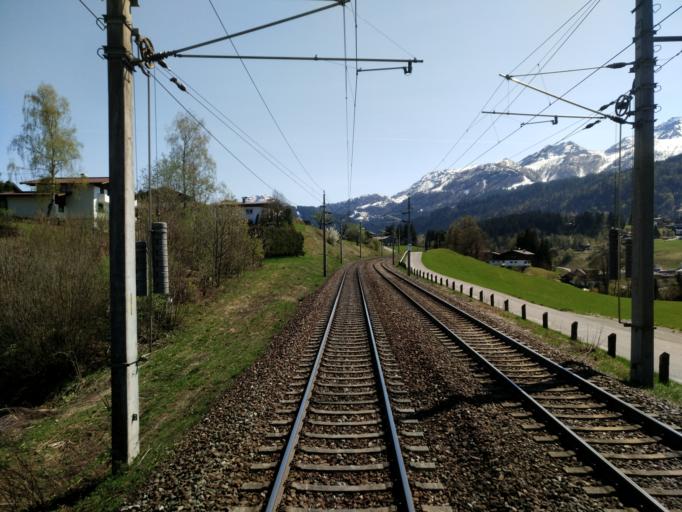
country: AT
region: Tyrol
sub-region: Politischer Bezirk Kitzbuhel
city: Fieberbrunn
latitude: 47.4852
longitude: 12.5382
